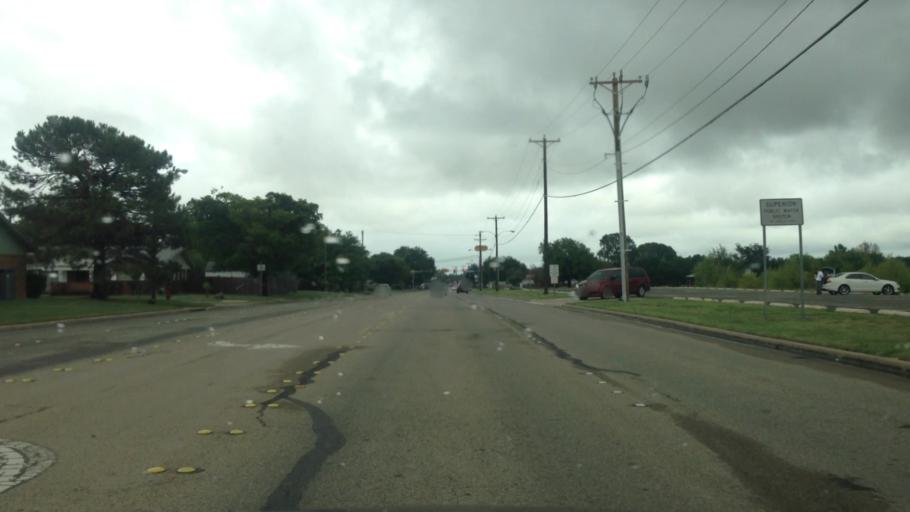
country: US
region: Texas
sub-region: Tarrant County
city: White Settlement
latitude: 32.7662
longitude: -97.4749
